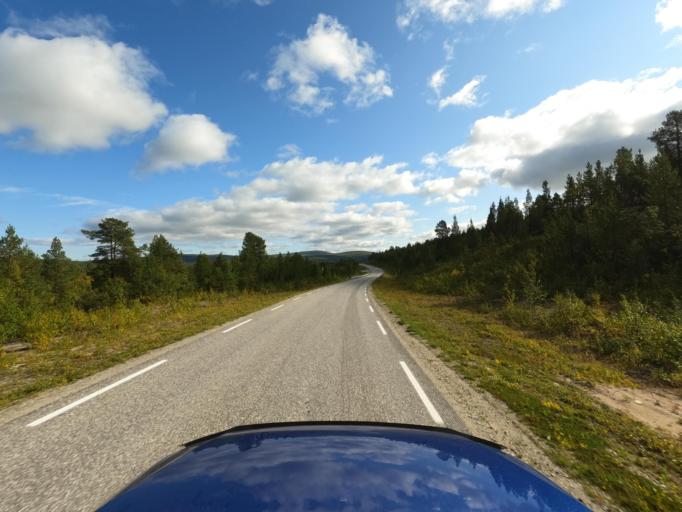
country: NO
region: Finnmark Fylke
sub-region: Karasjok
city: Karasjohka
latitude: 69.4327
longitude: 25.7255
